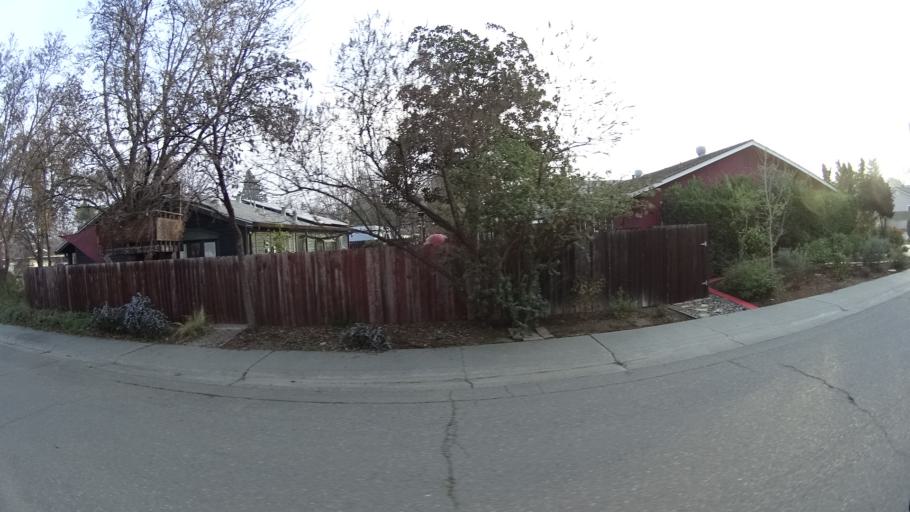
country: US
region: California
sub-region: Yolo County
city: Davis
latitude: 38.5657
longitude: -121.7467
